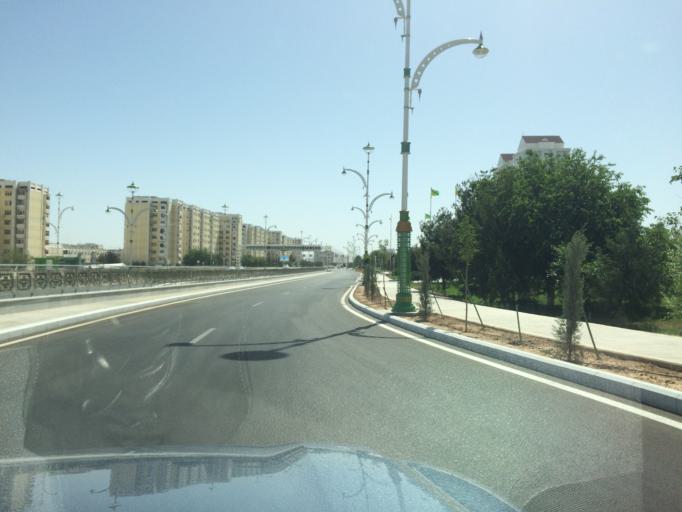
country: TM
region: Ahal
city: Ashgabat
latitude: 37.8953
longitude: 58.3889
